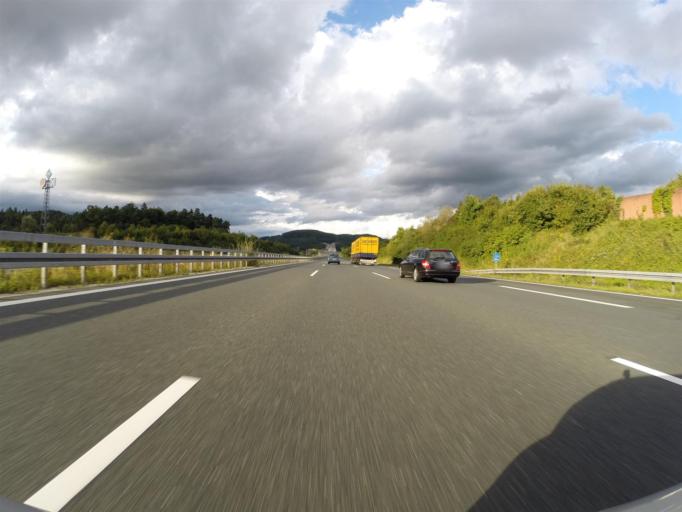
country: DE
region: Bavaria
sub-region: Regierungsbezirk Mittelfranken
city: Schnaittach
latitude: 49.5666
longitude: 11.3307
